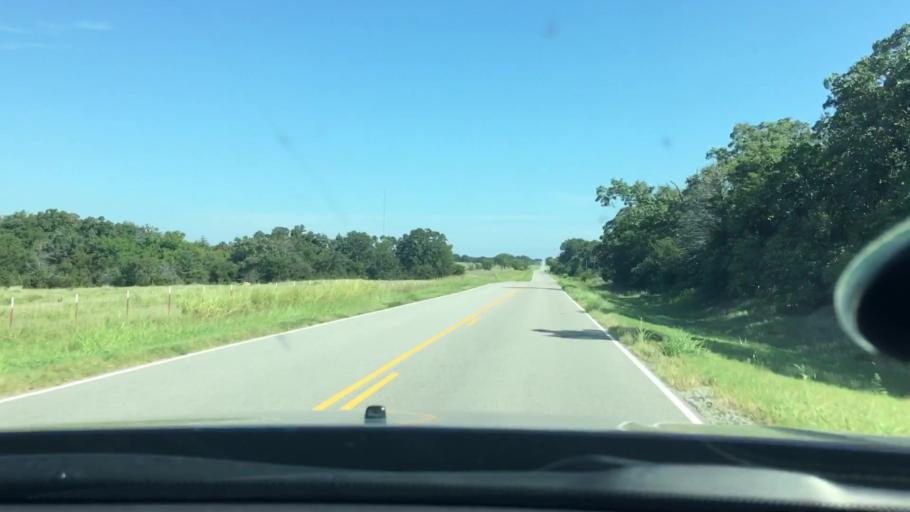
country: US
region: Oklahoma
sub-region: Johnston County
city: Tishomingo
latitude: 34.3112
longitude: -96.5488
